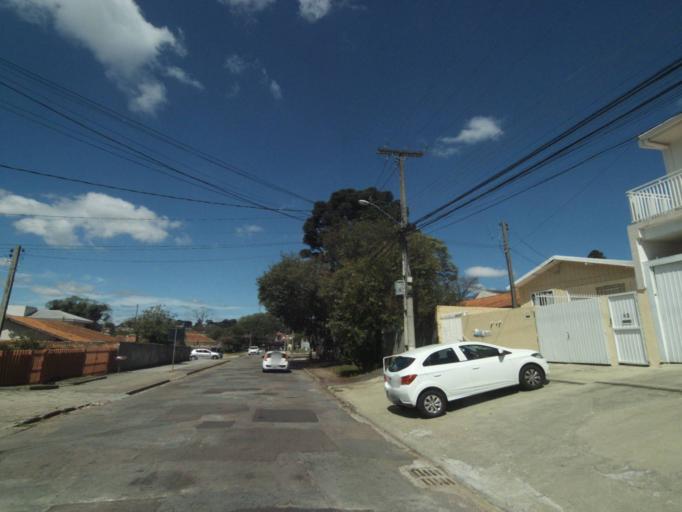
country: BR
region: Parana
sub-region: Curitiba
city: Curitiba
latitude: -25.3990
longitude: -49.2731
